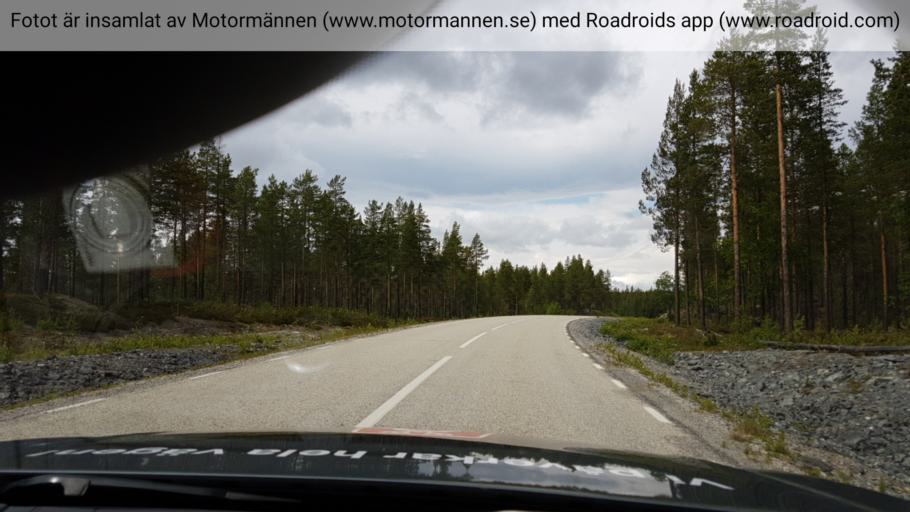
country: SE
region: Jaemtland
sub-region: Are Kommun
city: Jarpen
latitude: 62.8379
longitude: 13.4159
